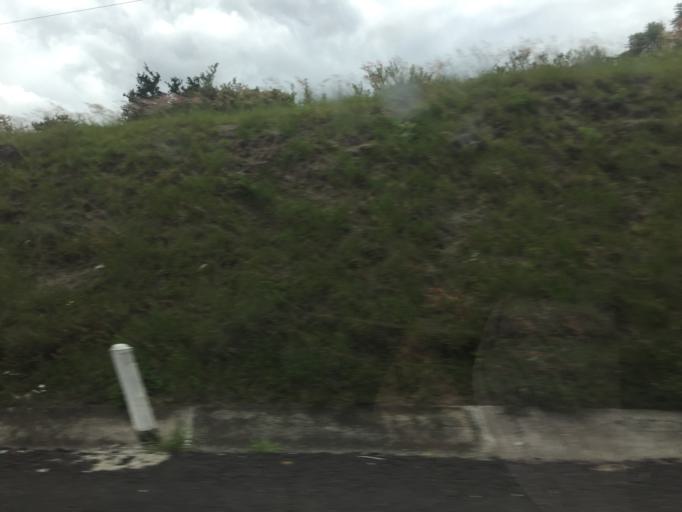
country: MX
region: Jalisco
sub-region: Zapotlanejo
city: La Mezquitera
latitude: 20.5992
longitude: -103.1163
